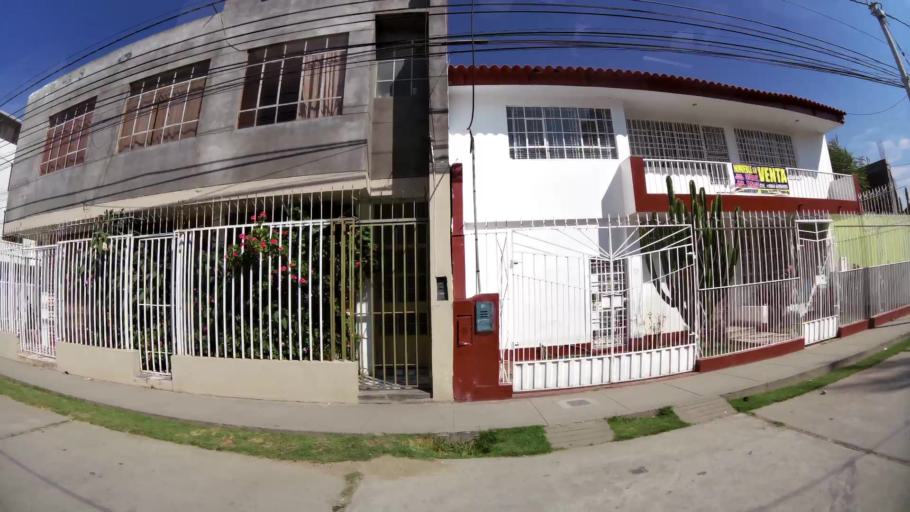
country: PE
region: Junin
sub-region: Provincia de Huancayo
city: El Tambo
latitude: -12.0782
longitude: -75.2286
